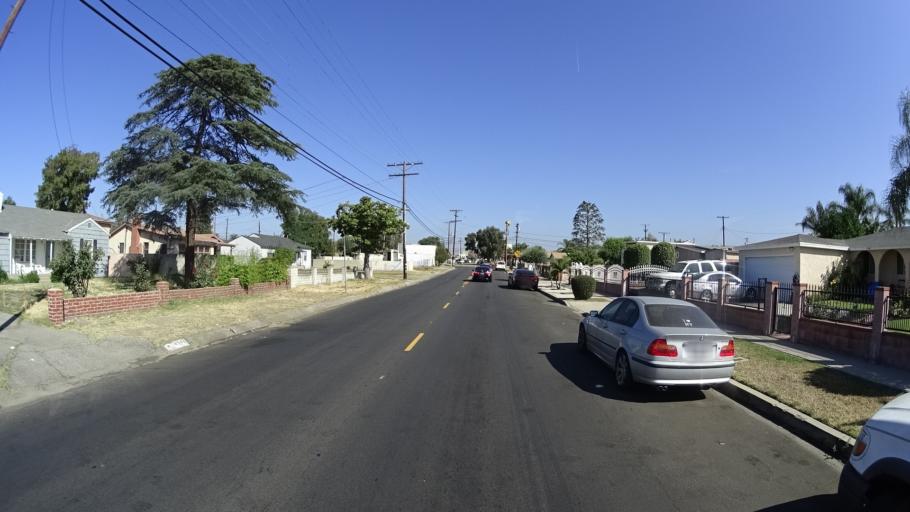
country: US
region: California
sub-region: Los Angeles County
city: Van Nuys
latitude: 34.2253
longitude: -118.4316
